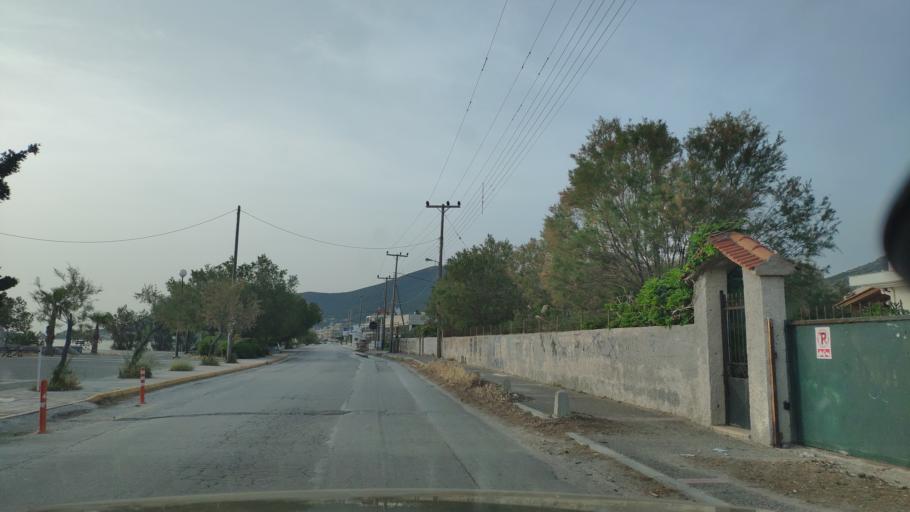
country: GR
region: Attica
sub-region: Nomarchia Anatolikis Attikis
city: Limin Mesoyaias
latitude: 37.8744
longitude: 24.0182
